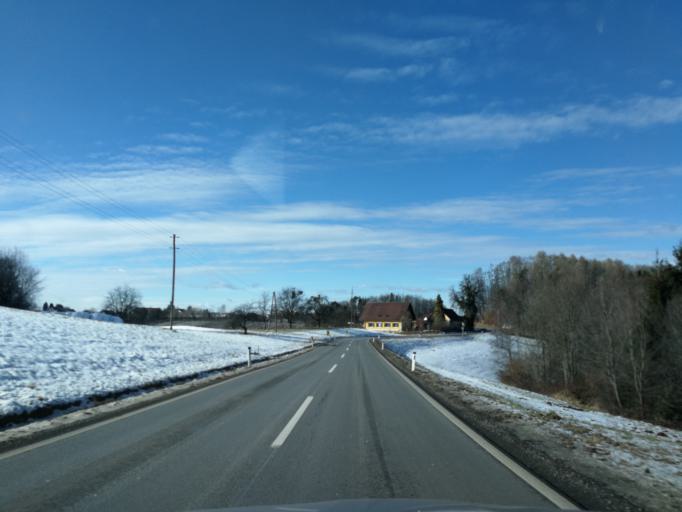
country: AT
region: Styria
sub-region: Politischer Bezirk Graz-Umgebung
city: Nestelbach bei Graz
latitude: 47.0571
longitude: 15.6193
